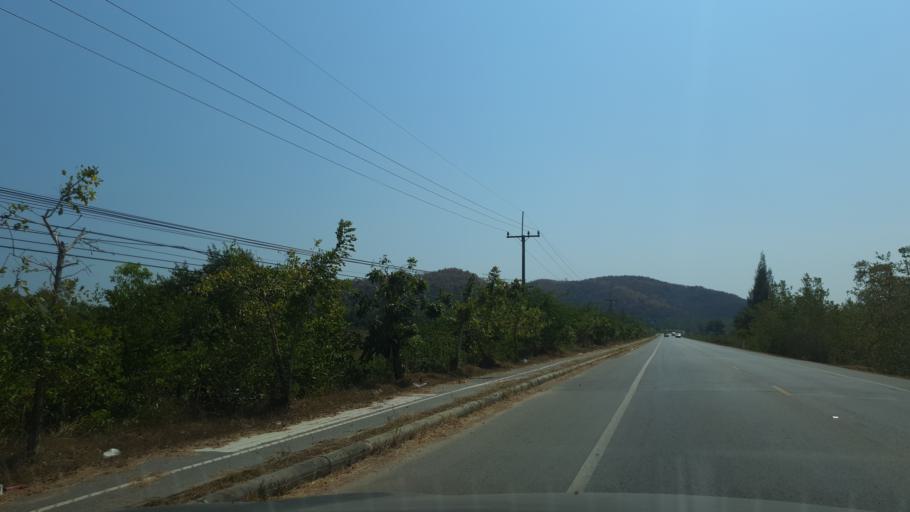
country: TH
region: Prachuap Khiri Khan
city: Pran Buri
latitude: 12.3228
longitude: 99.9596
